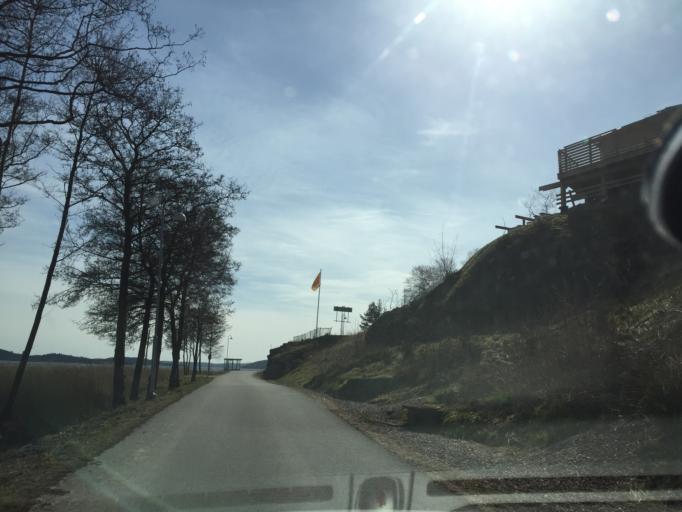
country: SE
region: Vaestra Goetaland
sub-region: Orust
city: Henan
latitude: 58.3415
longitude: 11.7297
